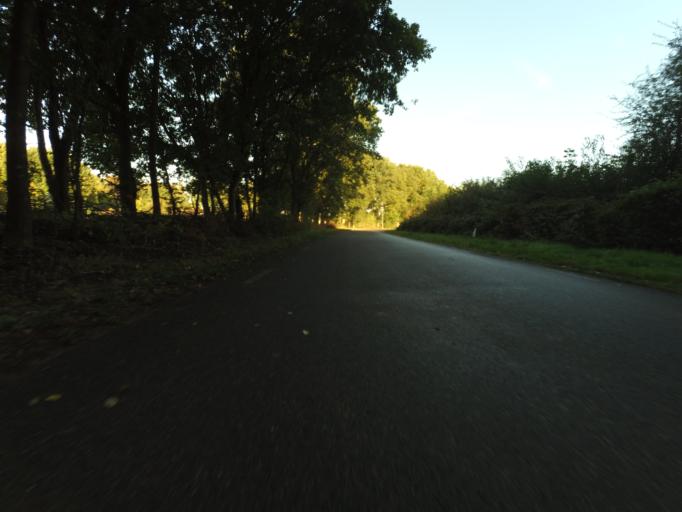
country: NL
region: Gelderland
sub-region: Gemeente Apeldoorn
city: Uddel
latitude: 52.2882
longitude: 5.7946
